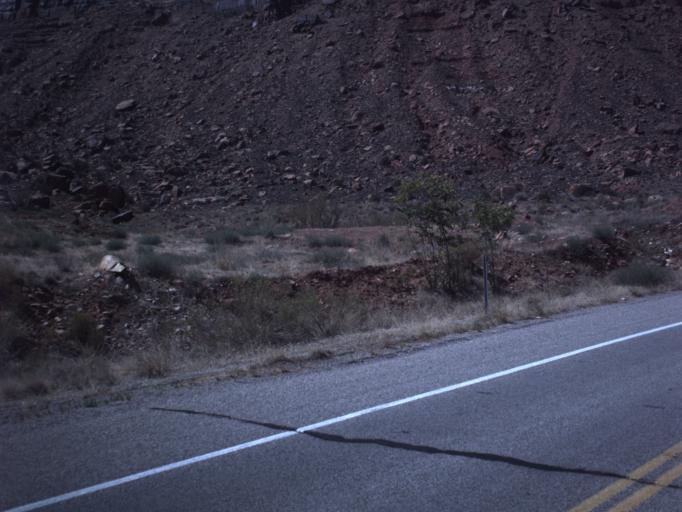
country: US
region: Utah
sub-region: Grand County
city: Moab
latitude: 38.6778
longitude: -109.4505
